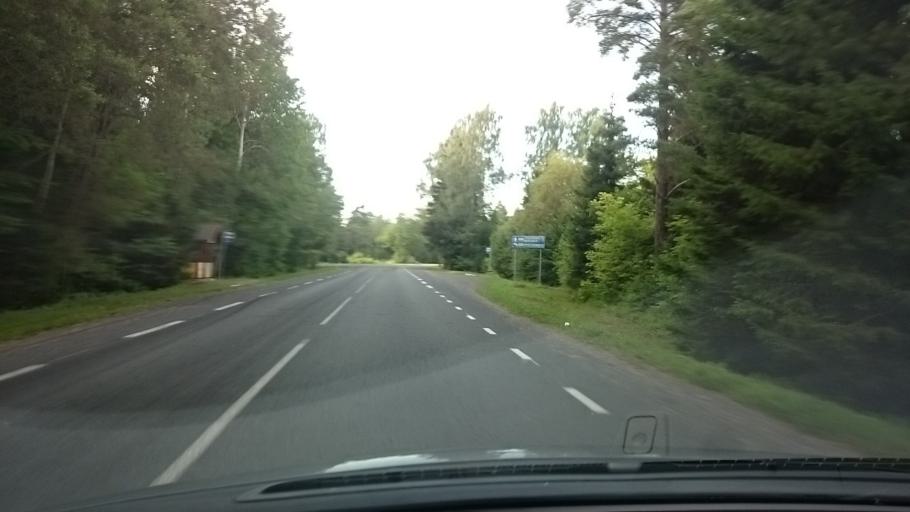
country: EE
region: Saare
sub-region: Kuressaare linn
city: Kuressaare
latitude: 58.4457
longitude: 22.2439
